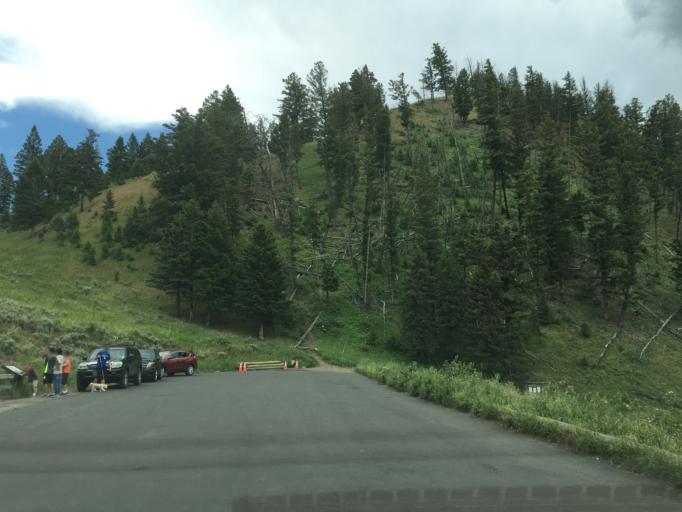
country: US
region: Montana
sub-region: Gallatin County
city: West Yellowstone
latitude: 44.9157
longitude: -110.4387
